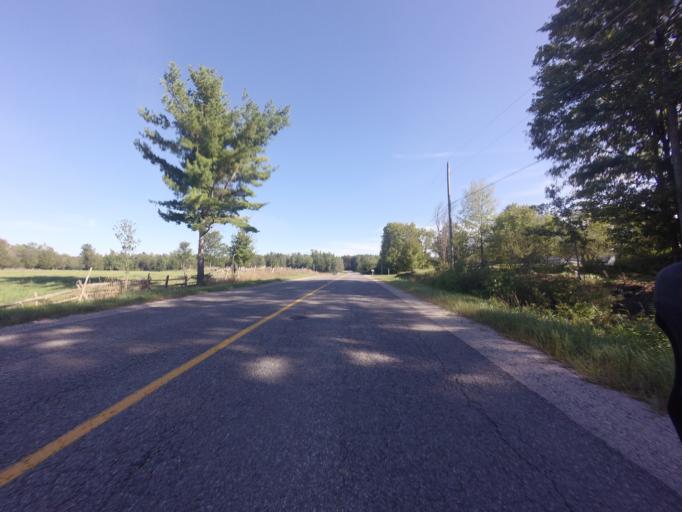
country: CA
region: Ontario
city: Perth
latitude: 44.9121
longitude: -76.3467
